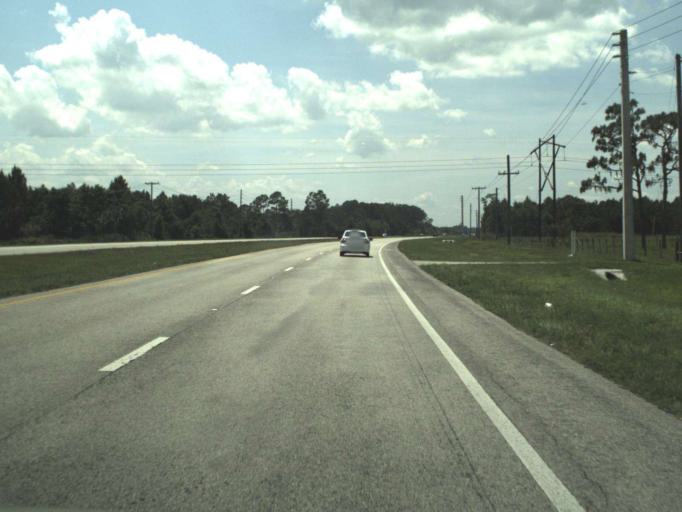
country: US
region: Florida
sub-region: Volusia County
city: Samsula-Spruce Creek
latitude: 29.0117
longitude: -81.0821
